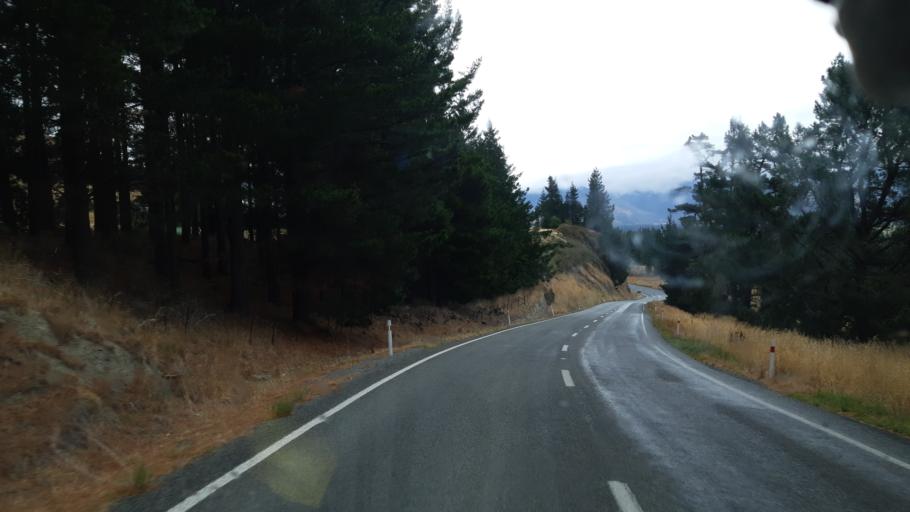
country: NZ
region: Canterbury
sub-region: Hurunui District
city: Amberley
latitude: -42.5823
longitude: 172.7754
